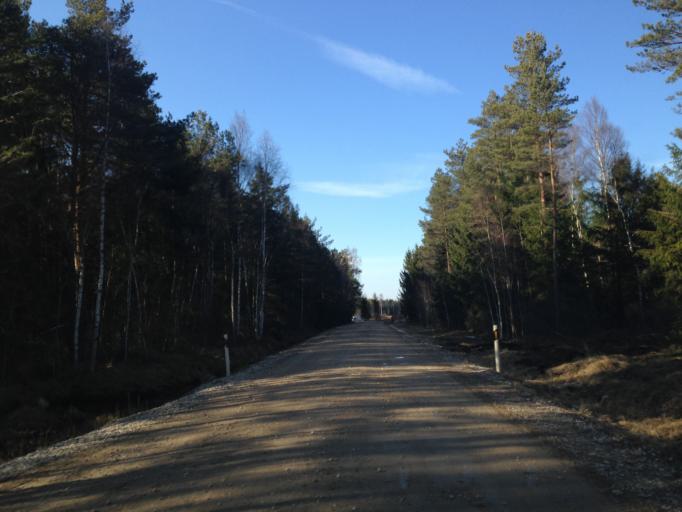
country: EE
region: Harju
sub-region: Nissi vald
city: Turba
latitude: 59.1572
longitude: 24.1440
